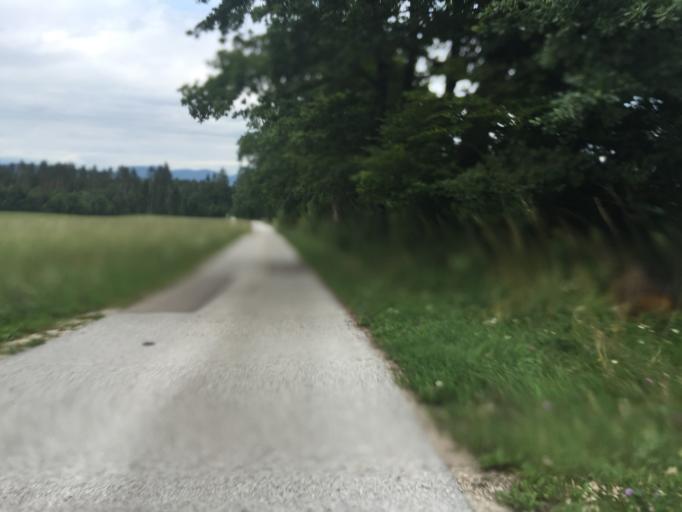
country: AT
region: Carinthia
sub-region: Politischer Bezirk Volkermarkt
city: Feistritz ob Bleiburg
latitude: 46.5467
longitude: 14.7885
